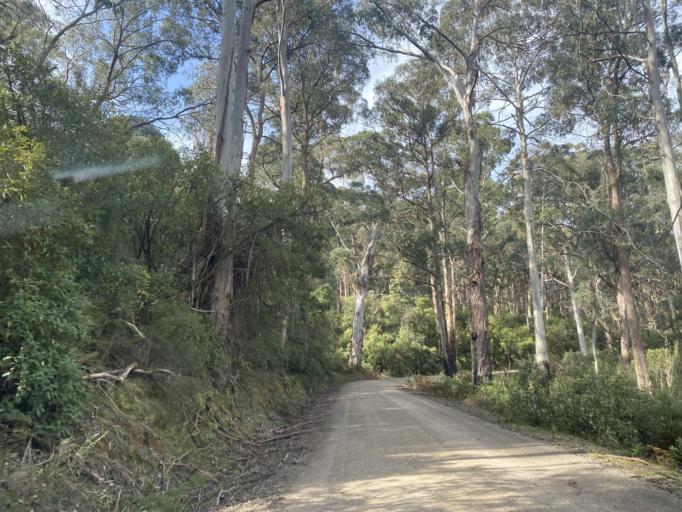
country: AU
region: Victoria
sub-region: Mansfield
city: Mansfield
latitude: -36.8440
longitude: 146.1726
